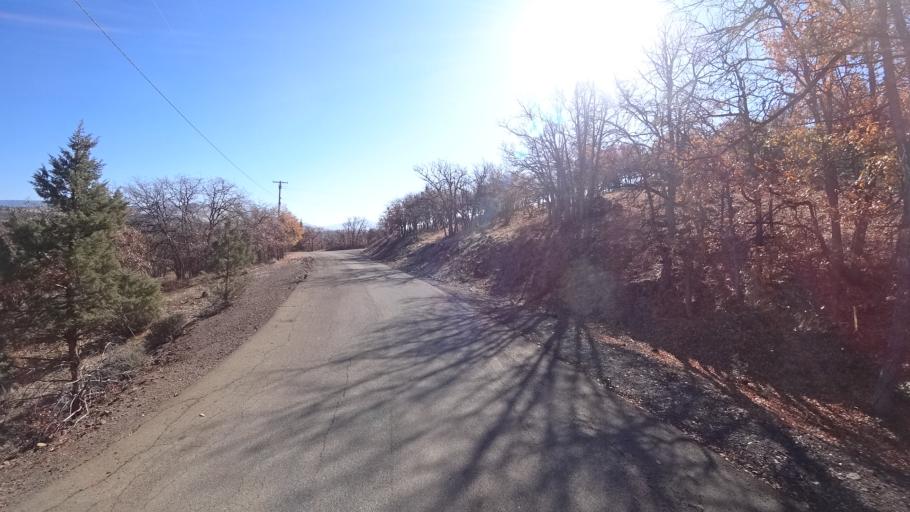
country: US
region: California
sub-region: Siskiyou County
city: Montague
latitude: 41.8751
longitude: -122.4812
